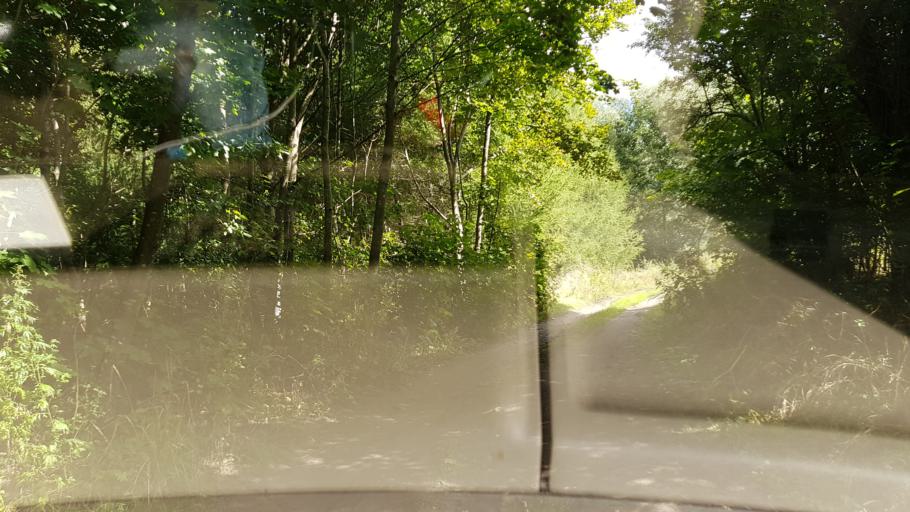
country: PL
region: West Pomeranian Voivodeship
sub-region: Powiat bialogardzki
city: Tychowo
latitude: 54.0053
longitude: 16.3201
